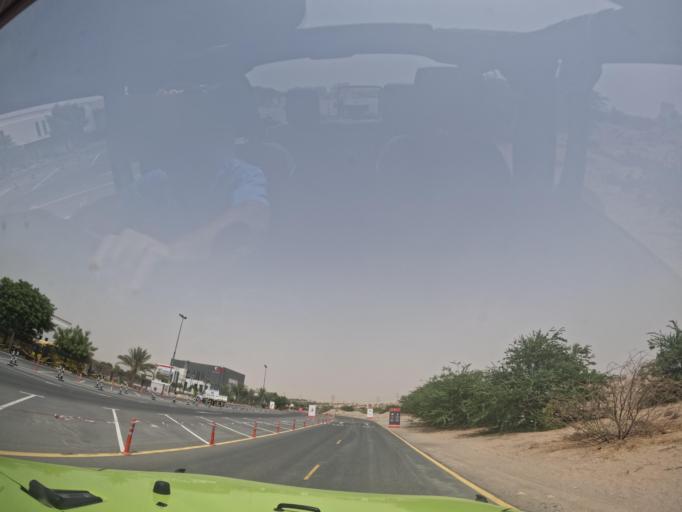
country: AE
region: Dubai
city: Dubai
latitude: 25.1050
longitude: 55.4000
